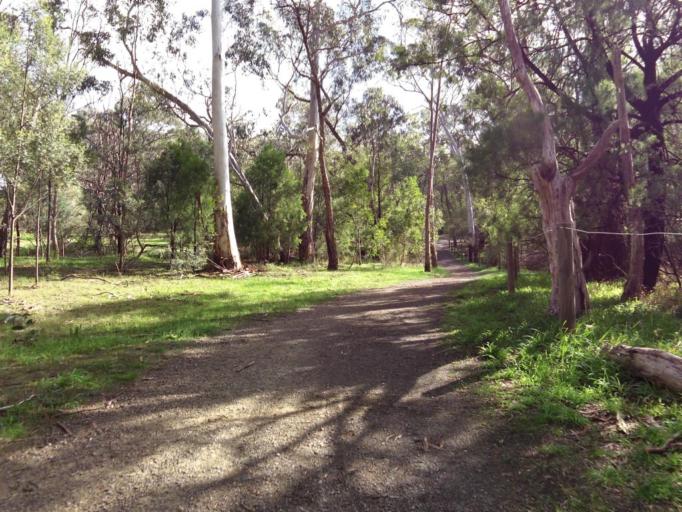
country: AU
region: Victoria
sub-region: Manningham
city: Park Orchards
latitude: -37.7771
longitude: 145.2216
